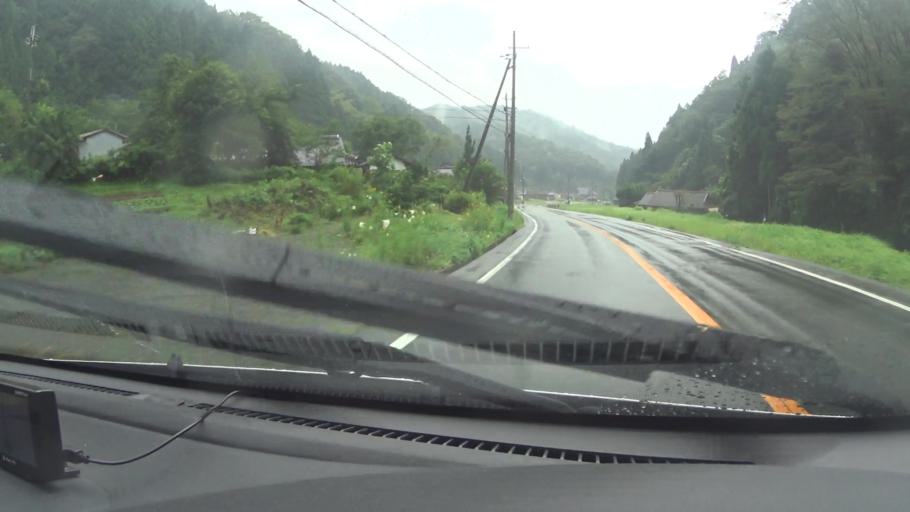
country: JP
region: Kyoto
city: Ayabe
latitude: 35.2339
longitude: 135.3316
